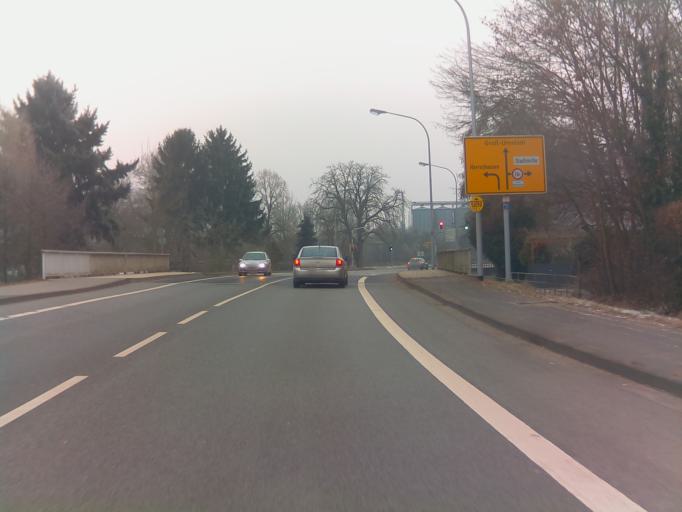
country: DE
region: Hesse
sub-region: Regierungsbezirk Darmstadt
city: Babenhausen
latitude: 49.9631
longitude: 8.9575
